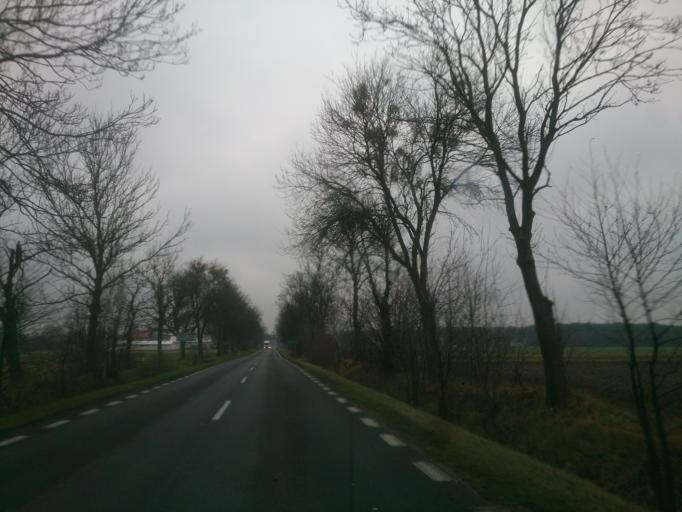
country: PL
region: Masovian Voivodeship
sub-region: Powiat sierpecki
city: Szczutowo
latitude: 52.9163
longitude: 19.6249
